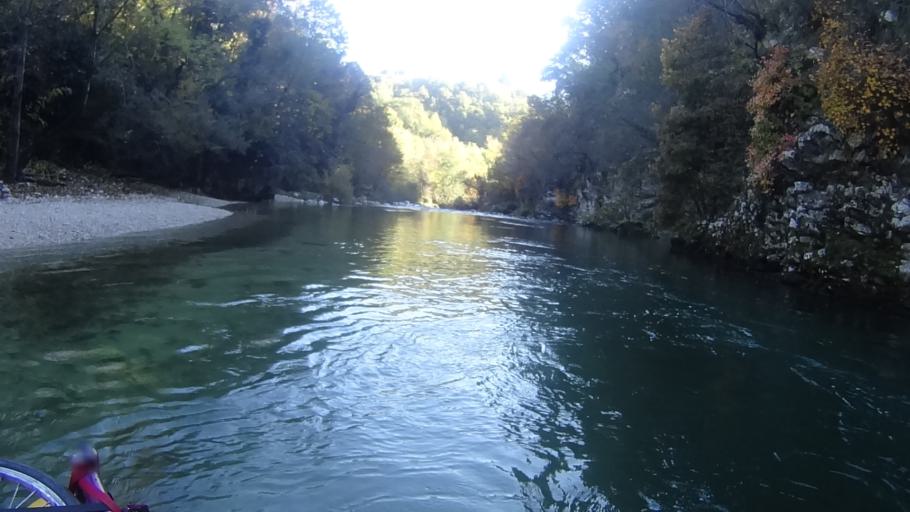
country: IT
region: Veneto
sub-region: Provincia di Vicenza
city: Chiuppano
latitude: 45.7684
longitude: 11.4600
